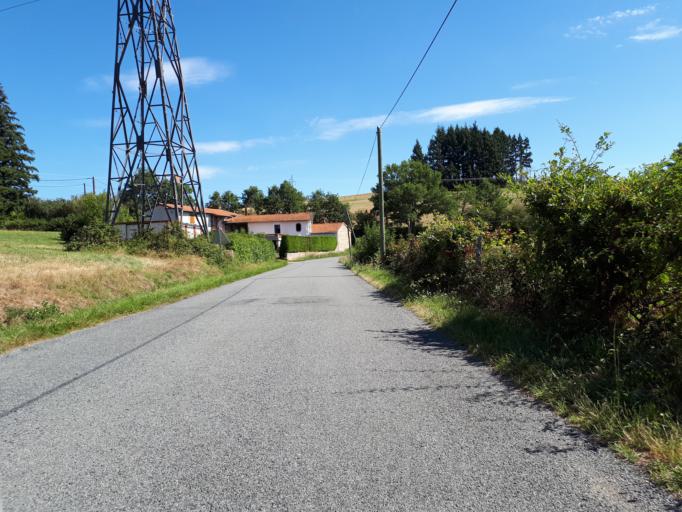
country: FR
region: Rhone-Alpes
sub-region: Departement de la Loire
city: Bussieres
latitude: 45.8317
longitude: 4.2748
